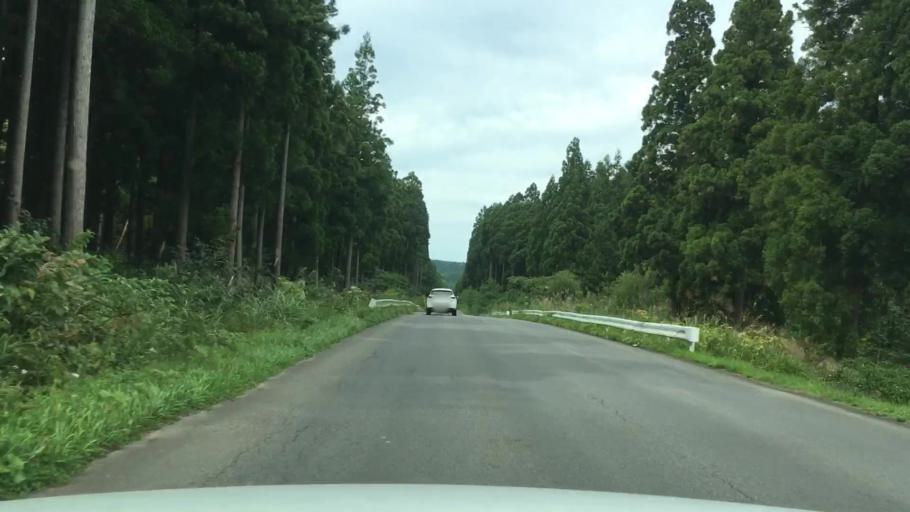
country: JP
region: Aomori
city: Shimokizukuri
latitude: 40.7106
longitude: 140.2724
